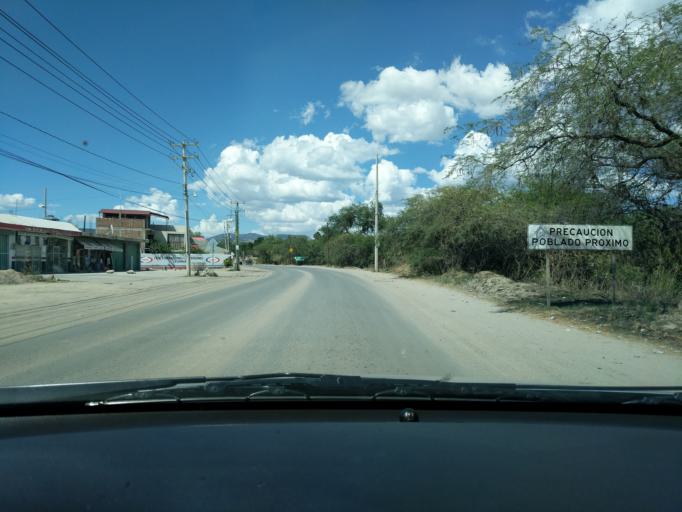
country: MX
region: Guanajuato
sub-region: Leon
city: Ladrilleras del Refugio
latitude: 21.0625
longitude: -101.5557
